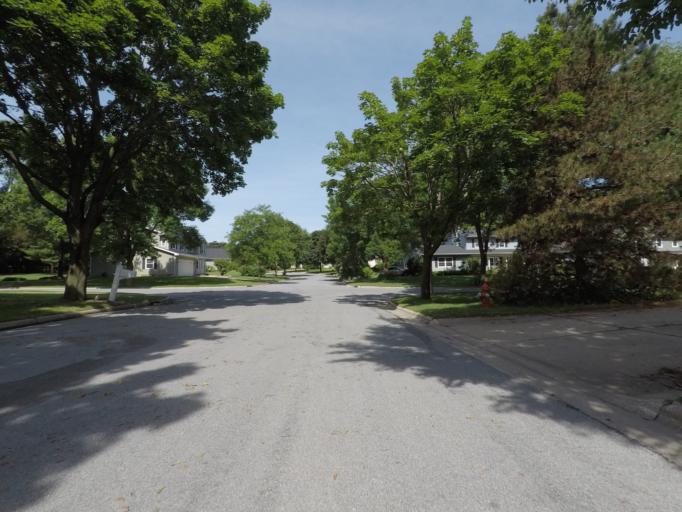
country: US
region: Wisconsin
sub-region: Dane County
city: Middleton
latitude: 43.0831
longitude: -89.5133
